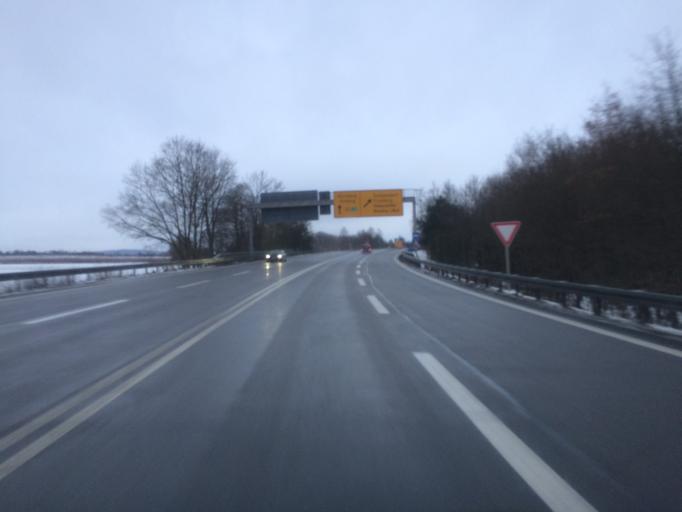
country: DE
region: Bavaria
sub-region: Upper Palatinate
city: Schwandorf in Bayern
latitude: 49.3440
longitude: 12.1456
